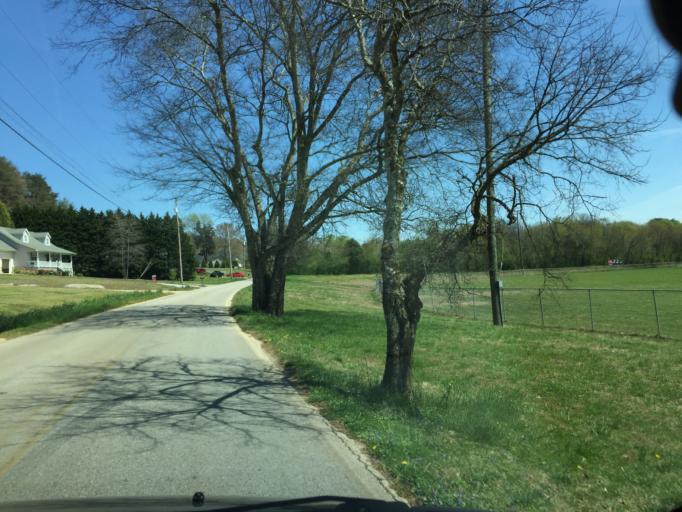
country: US
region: Tennessee
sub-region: Hamilton County
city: Soddy-Daisy
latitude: 35.2315
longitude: -85.2128
